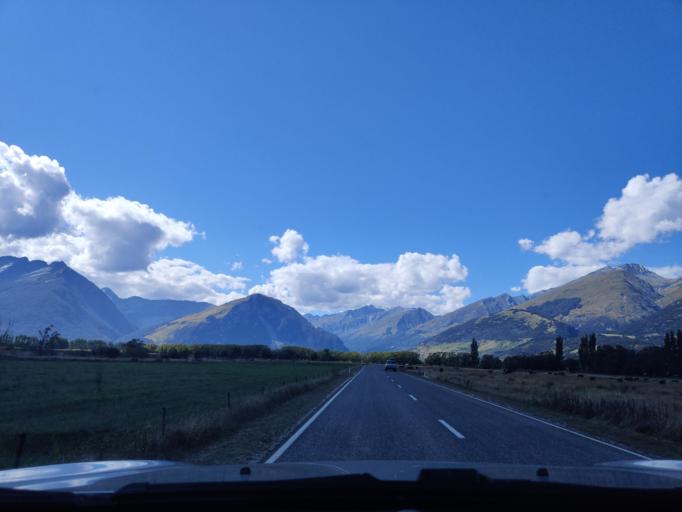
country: NZ
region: Otago
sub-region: Queenstown-Lakes District
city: Queenstown
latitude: -44.7855
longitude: 168.3904
